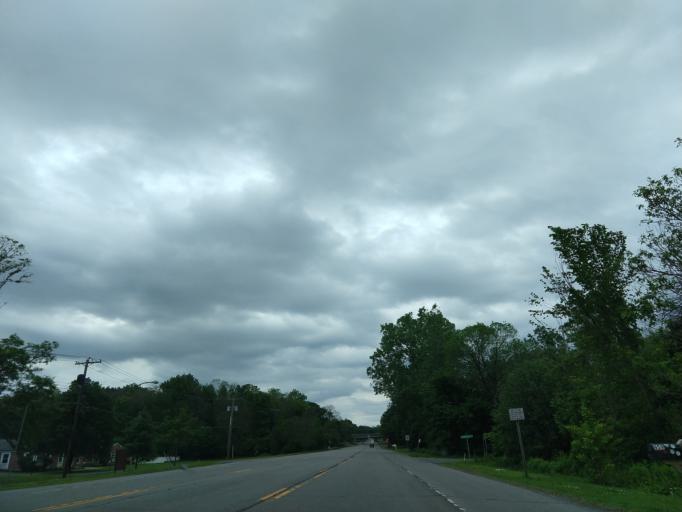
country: US
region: New York
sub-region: Erie County
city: East Aurora
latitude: 42.7676
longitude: -78.5989
